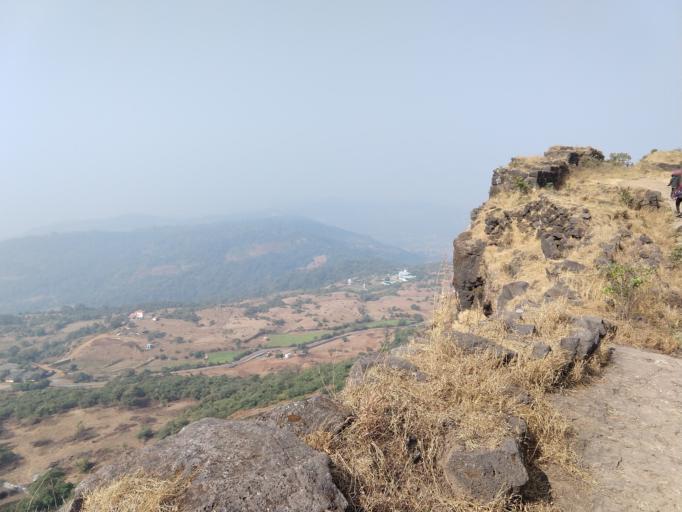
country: IN
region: Maharashtra
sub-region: Pune Division
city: Lonavla
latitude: 18.7132
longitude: 73.4708
